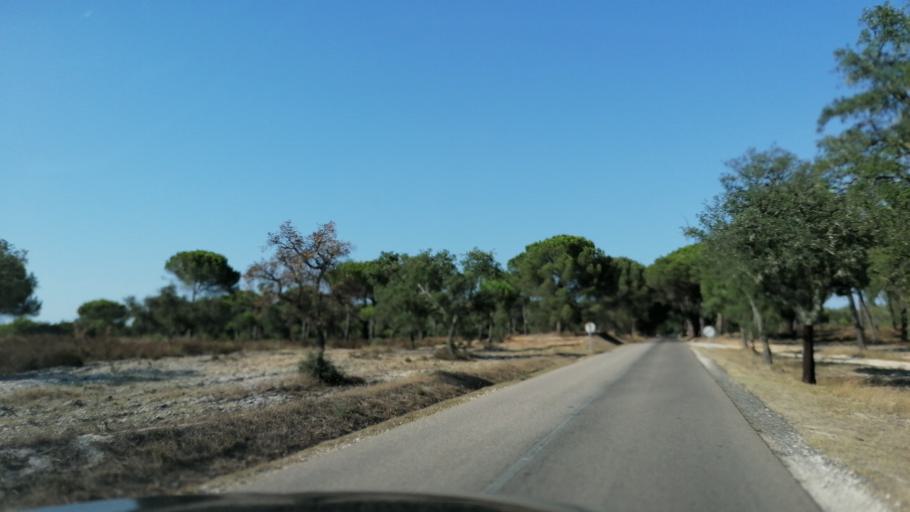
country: PT
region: Santarem
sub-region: Coruche
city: Coruche
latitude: 38.8361
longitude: -8.5586
